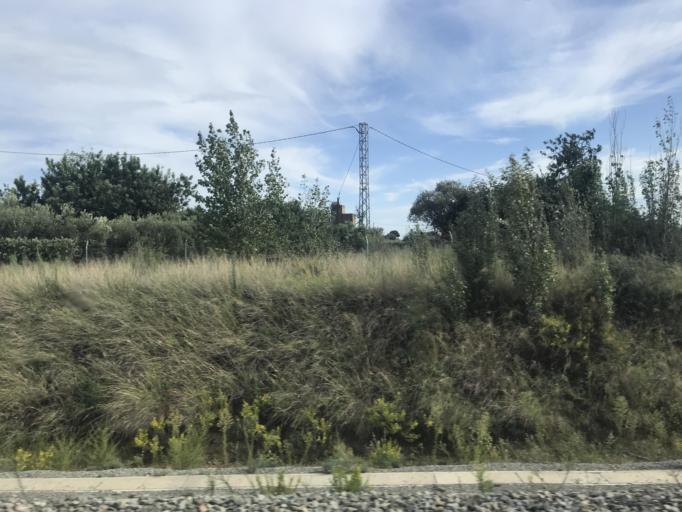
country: ES
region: Catalonia
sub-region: Provincia de Tarragona
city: Cambrils
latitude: 41.1000
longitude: 1.0942
